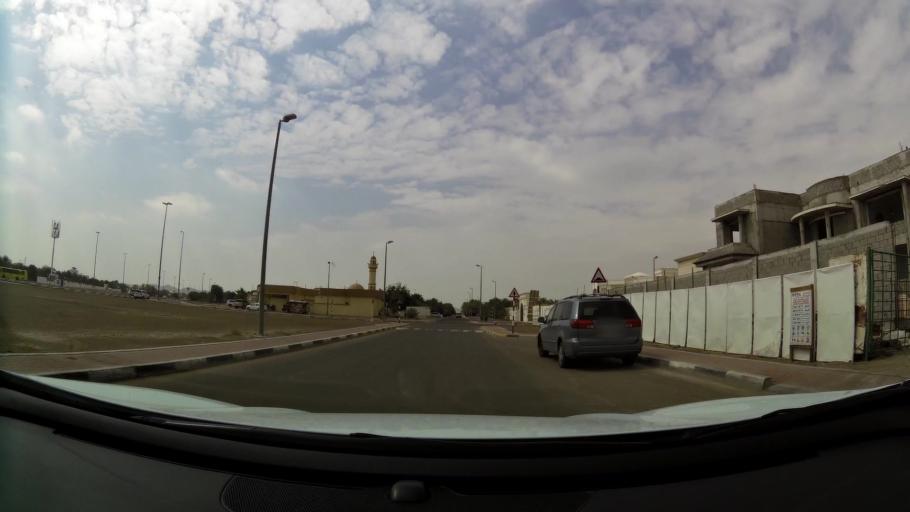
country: AE
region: Abu Dhabi
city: Al Ain
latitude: 24.1992
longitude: 55.8022
